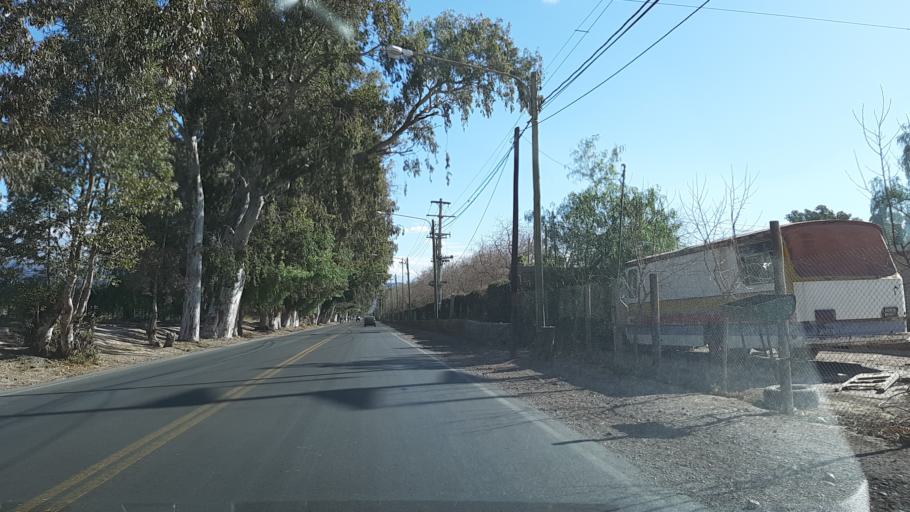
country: AR
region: San Juan
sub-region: Departamento de Rivadavia
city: Rivadavia
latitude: -31.5389
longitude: -68.6008
